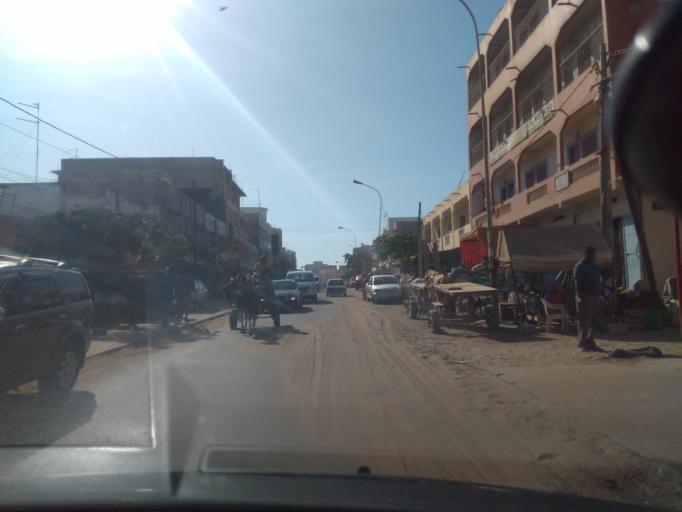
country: SN
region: Dakar
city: Pikine
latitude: 14.7592
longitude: -17.4319
